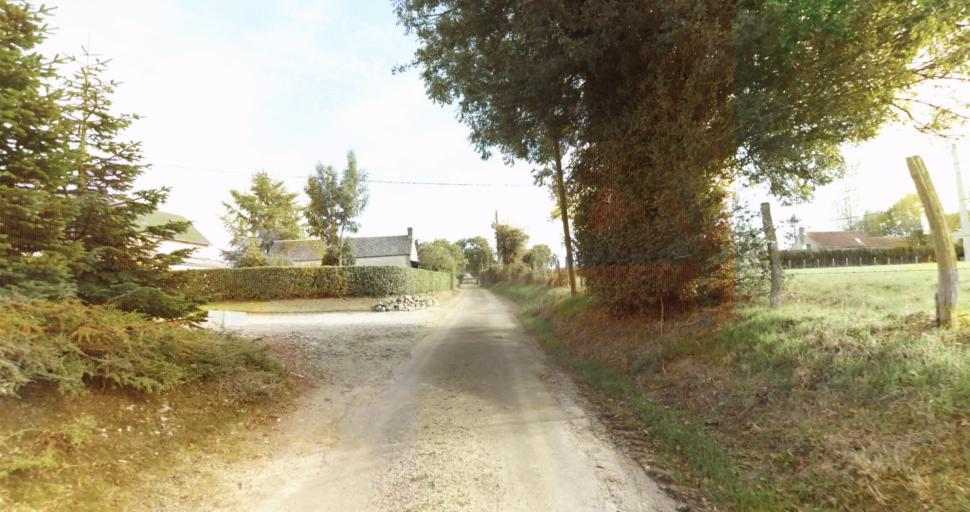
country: FR
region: Lower Normandy
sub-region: Departement de l'Orne
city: Gace
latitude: 48.7086
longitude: 0.2777
